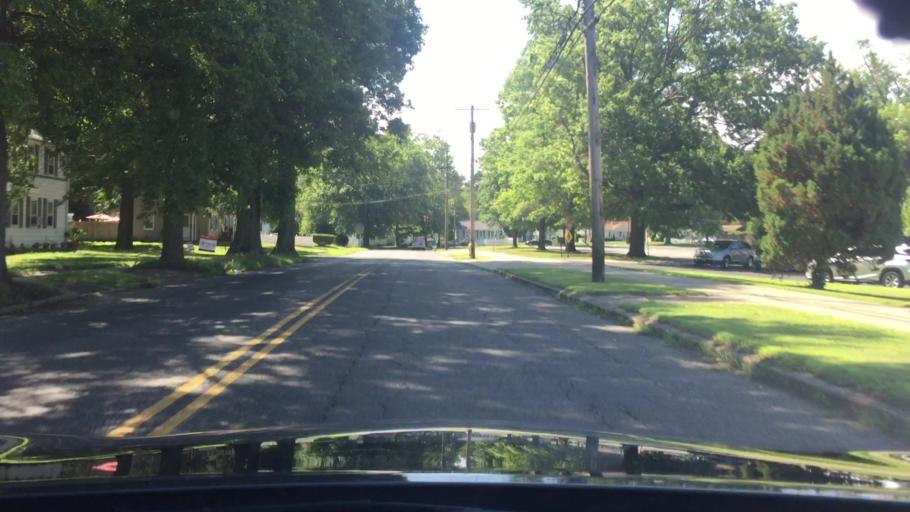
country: US
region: Connecticut
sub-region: New Haven County
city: City of Milford (balance)
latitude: 41.2043
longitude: -73.0881
